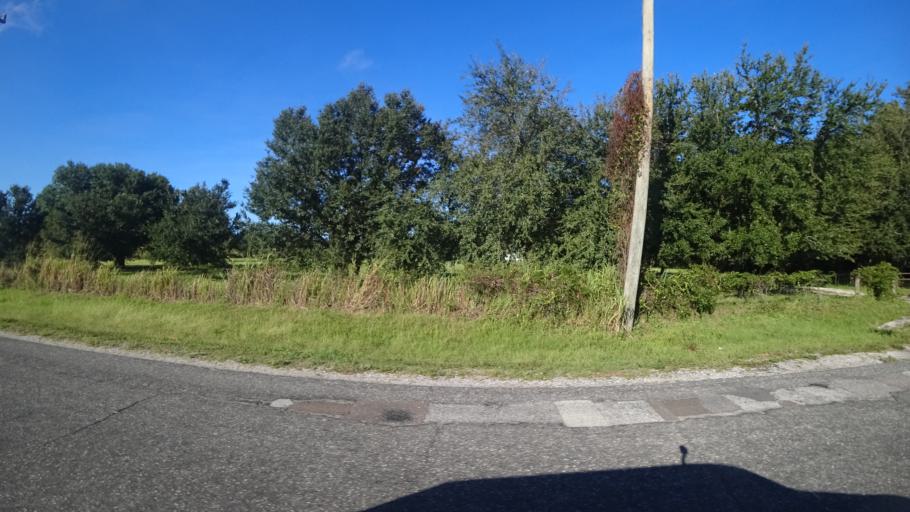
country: US
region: Florida
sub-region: Manatee County
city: Memphis
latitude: 27.5984
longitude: -82.5273
